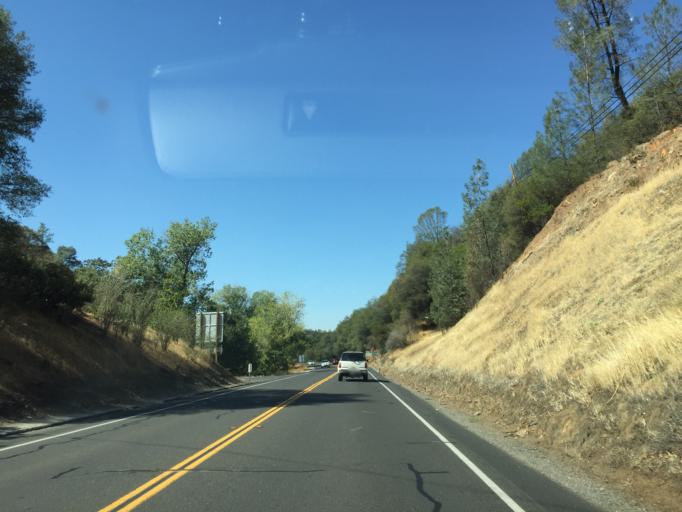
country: US
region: California
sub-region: Tuolumne County
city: Jamestown
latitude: 37.9626
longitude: -120.4072
